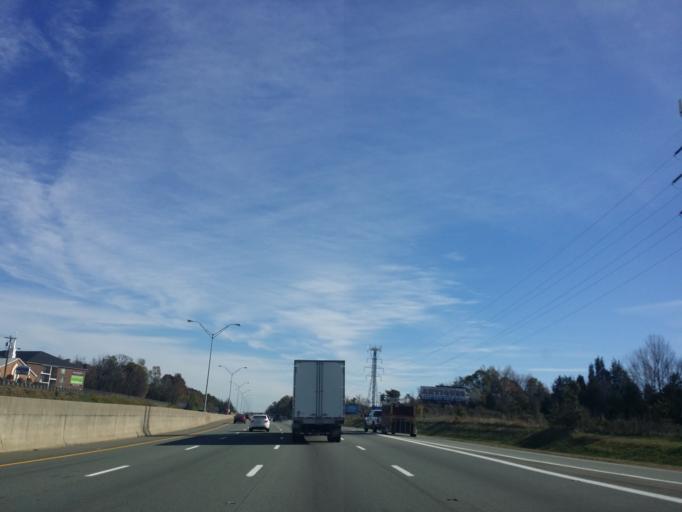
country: US
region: North Carolina
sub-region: Alamance County
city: Burlington
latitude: 36.0645
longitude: -79.4654
